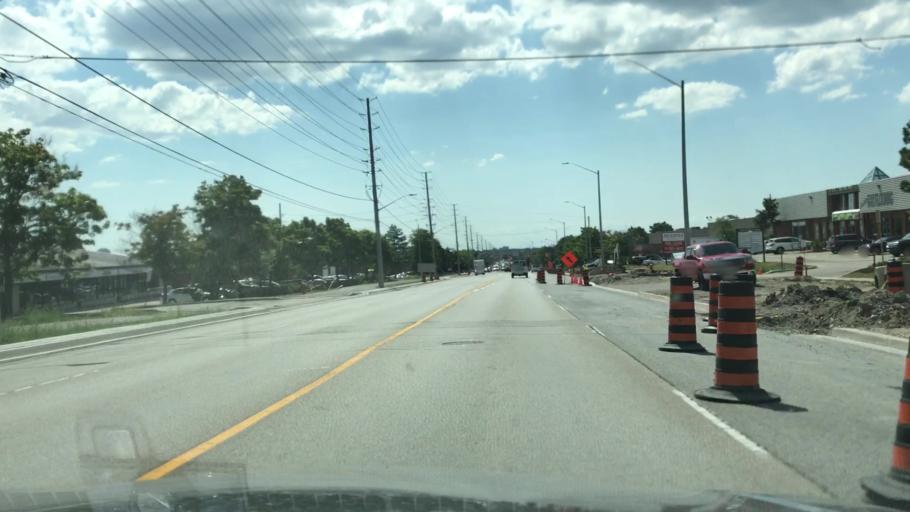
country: CA
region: Ontario
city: Mississauga
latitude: 43.6355
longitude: -79.6444
